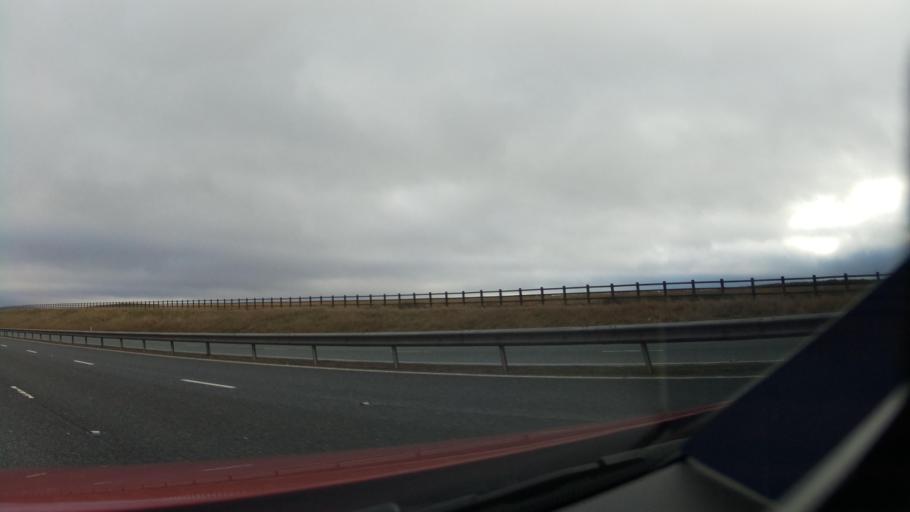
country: GB
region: Scotland
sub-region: South Lanarkshire
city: Douglas
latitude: 55.5219
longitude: -3.7468
